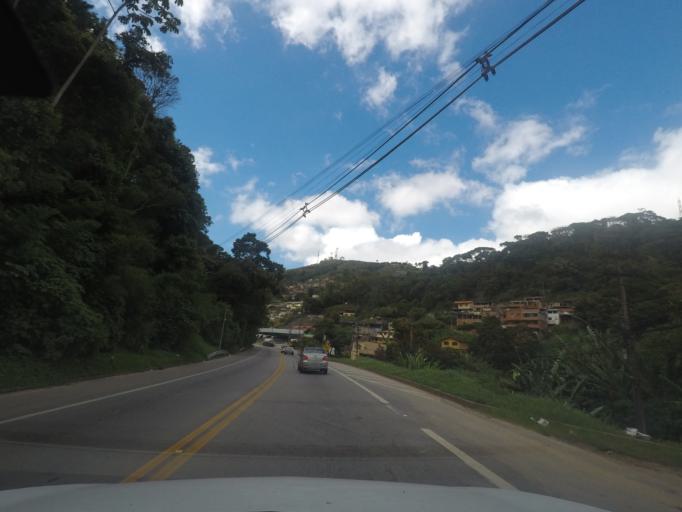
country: BR
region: Rio de Janeiro
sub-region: Teresopolis
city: Teresopolis
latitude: -22.3970
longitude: -42.9546
